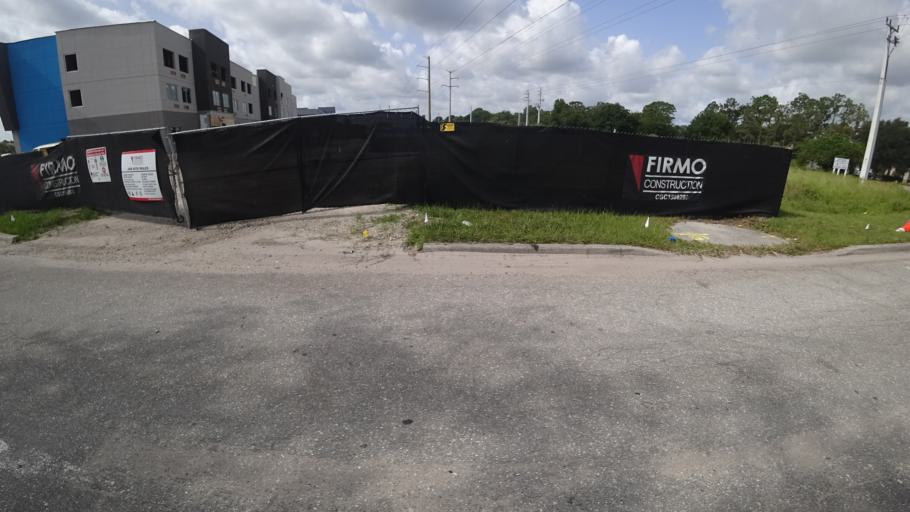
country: US
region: Florida
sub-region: Sarasota County
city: Desoto Lakes
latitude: 27.4425
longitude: -82.4676
